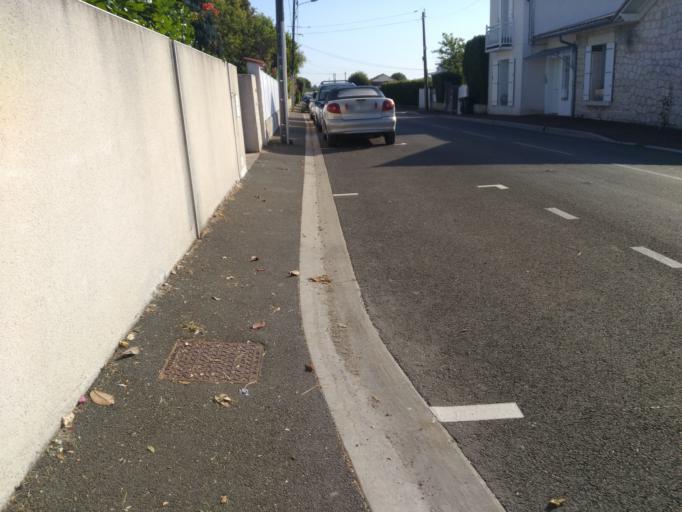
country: FR
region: Poitou-Charentes
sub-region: Departement de la Charente-Maritime
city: Saint-Palais-sur-Mer
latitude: 45.6435
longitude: -1.0823
